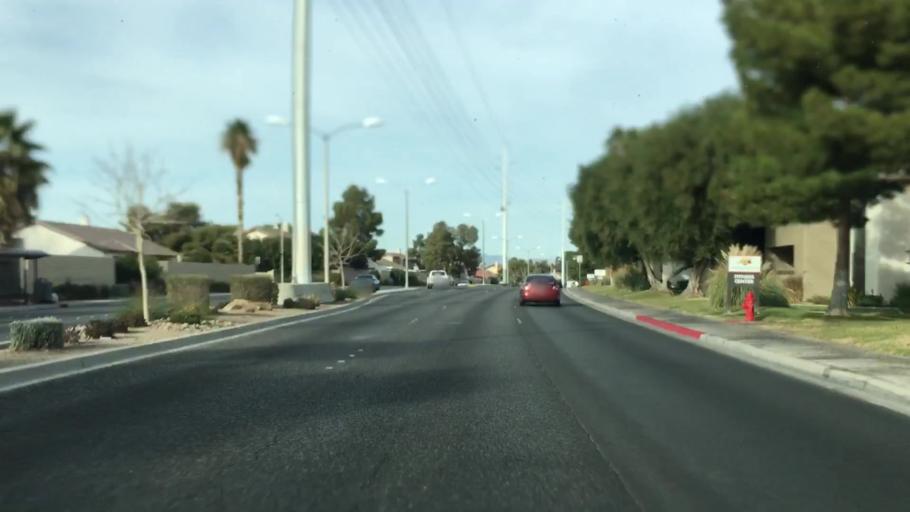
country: US
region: Nevada
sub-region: Clark County
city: Whitney
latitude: 36.0599
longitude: -115.0849
